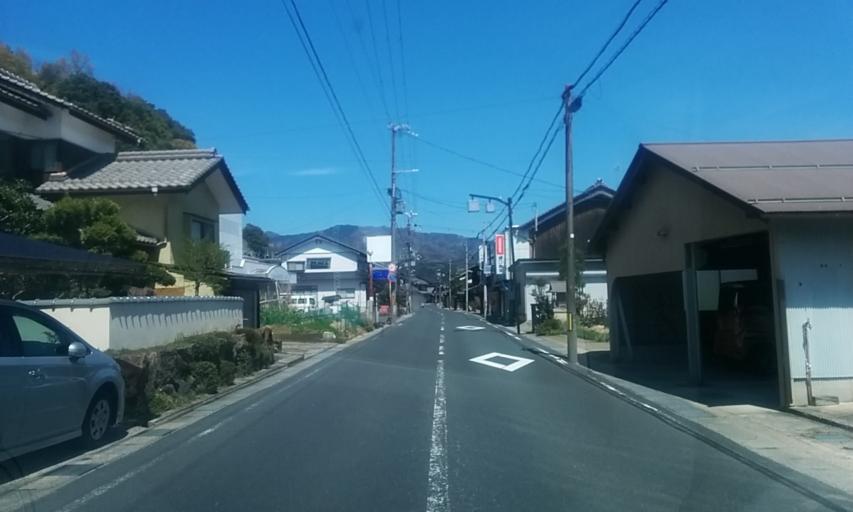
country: JP
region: Kyoto
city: Miyazu
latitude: 35.5636
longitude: 135.1477
